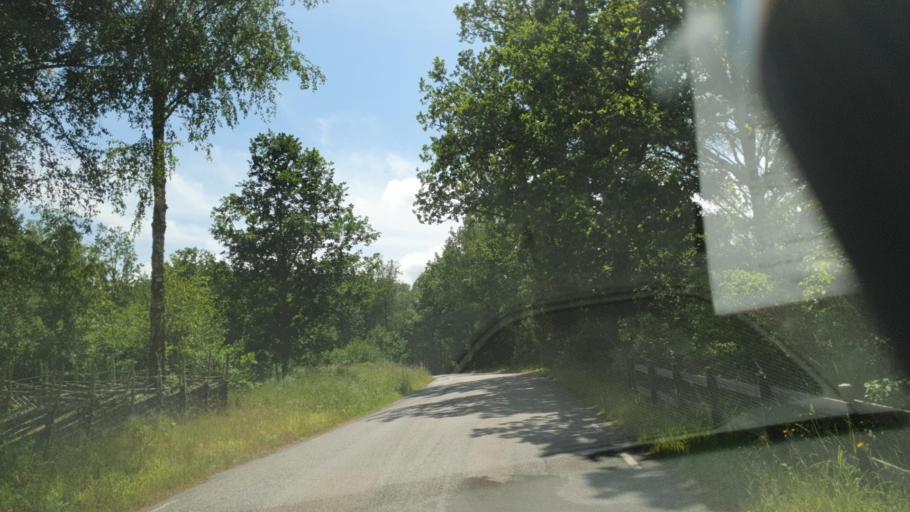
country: SE
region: Kronoberg
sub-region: Lessebo Kommun
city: Hovmantorp
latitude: 56.7460
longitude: 15.1763
